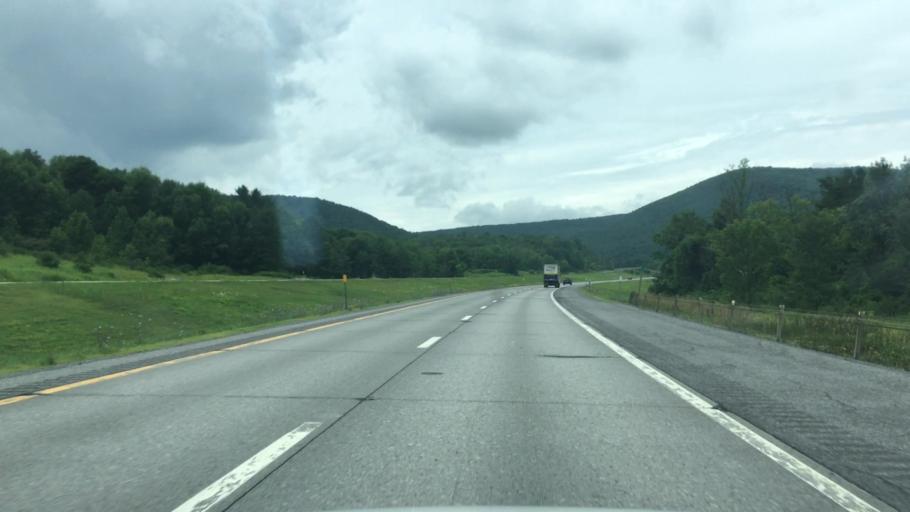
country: US
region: New York
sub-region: Schoharie County
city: Cobleskill
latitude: 42.6488
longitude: -74.6138
